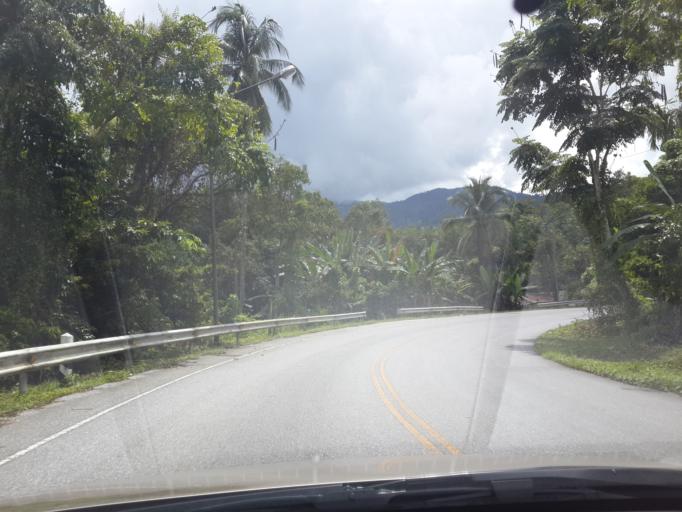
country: TH
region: Yala
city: Raman
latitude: 6.3800
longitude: 101.3930
